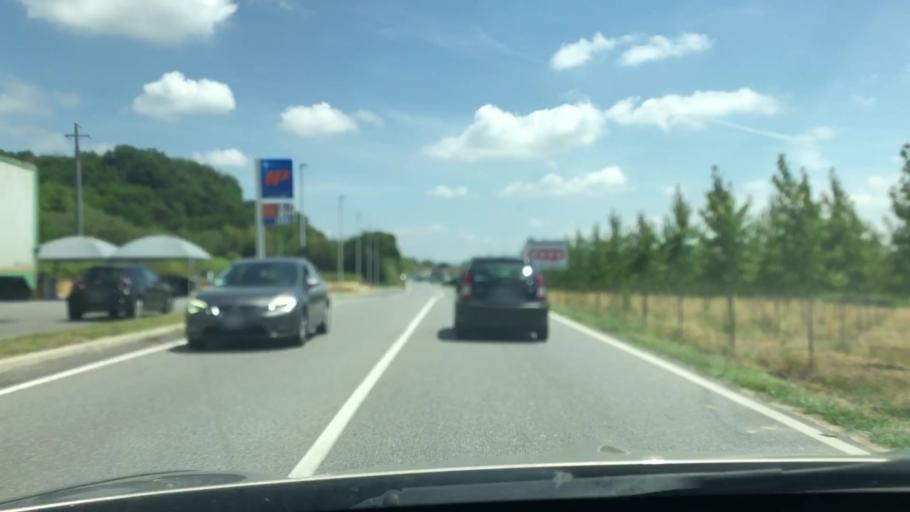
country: IT
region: Tuscany
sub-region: Province of Pisa
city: Treggiaia
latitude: 43.6130
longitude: 10.6830
